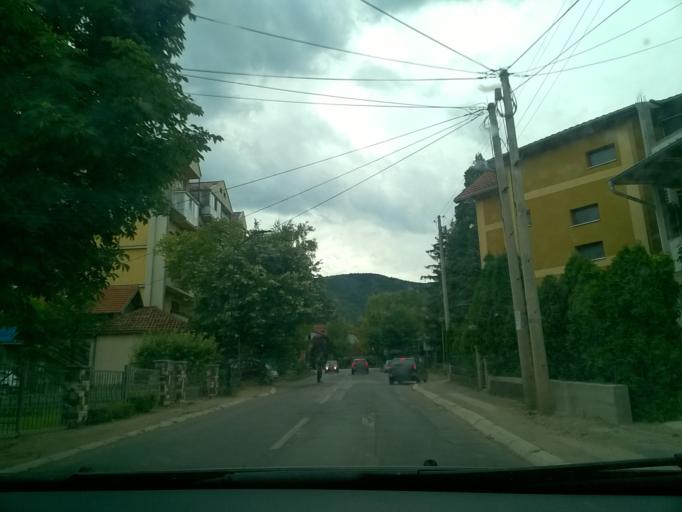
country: RS
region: Central Serbia
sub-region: Zajecarski Okrug
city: Soko Banja
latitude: 43.6460
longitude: 21.8678
